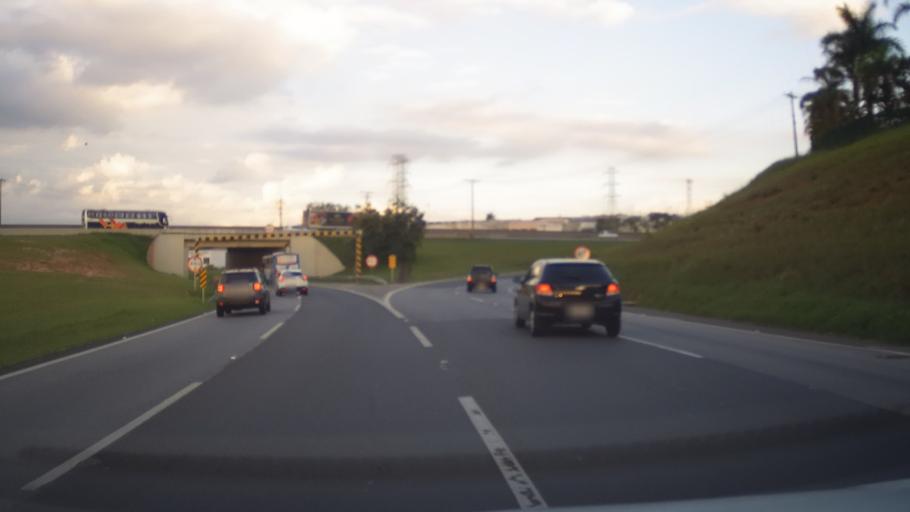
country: BR
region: Sao Paulo
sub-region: Campinas
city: Campinas
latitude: -22.9345
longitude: -47.0737
